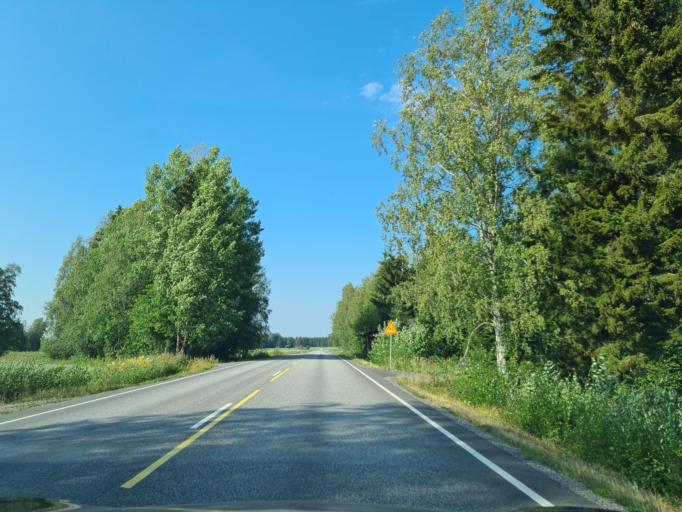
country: FI
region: Satakunta
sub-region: Pohjois-Satakunta
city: Kankaanpaeae
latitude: 61.9049
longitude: 22.4988
